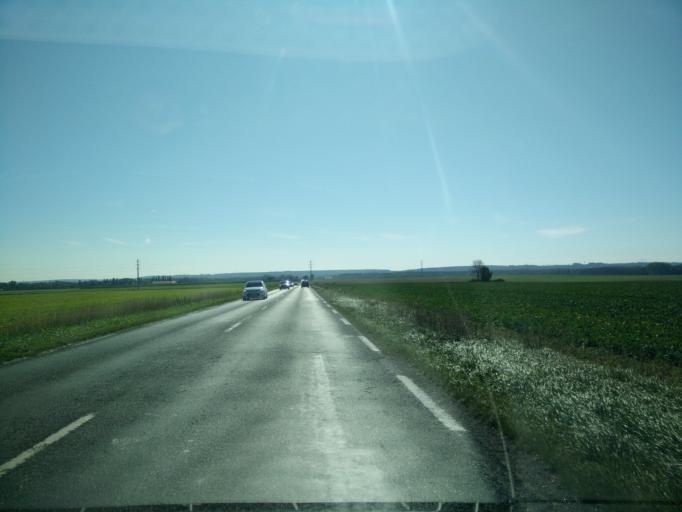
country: FR
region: Ile-de-France
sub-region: Departement de Seine-et-Marne
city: Mitry-Mory
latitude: 48.9797
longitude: 2.6597
